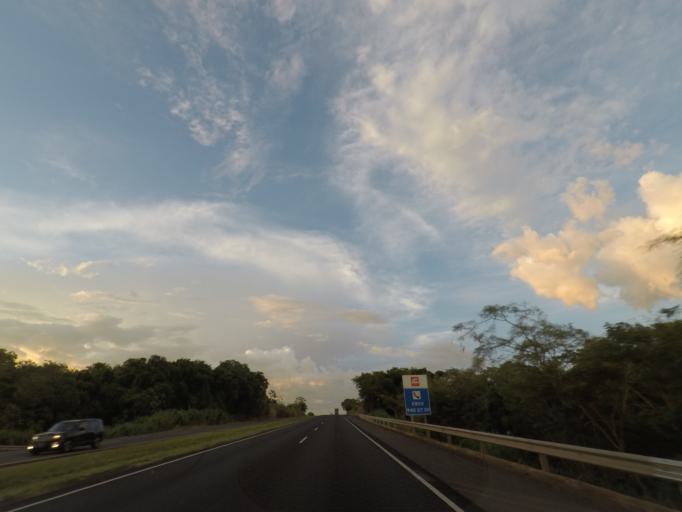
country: BR
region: Minas Gerais
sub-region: Uberaba
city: Uberaba
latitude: -19.6874
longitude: -47.9918
